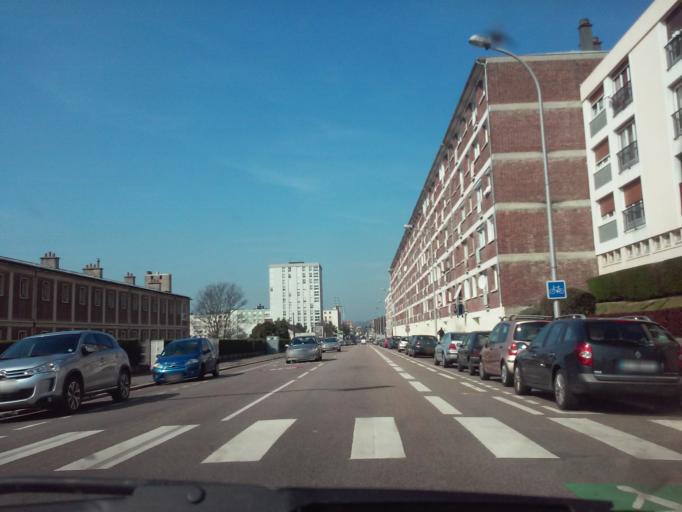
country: FR
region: Haute-Normandie
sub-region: Departement de la Seine-Maritime
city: Harfleur
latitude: 49.5024
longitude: 0.1792
